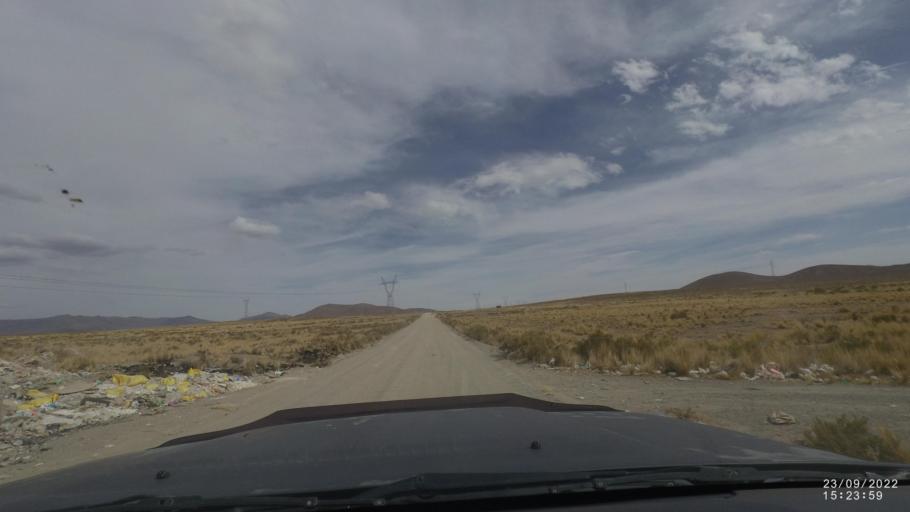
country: BO
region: Oruro
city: Oruro
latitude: -17.9313
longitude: -67.0409
